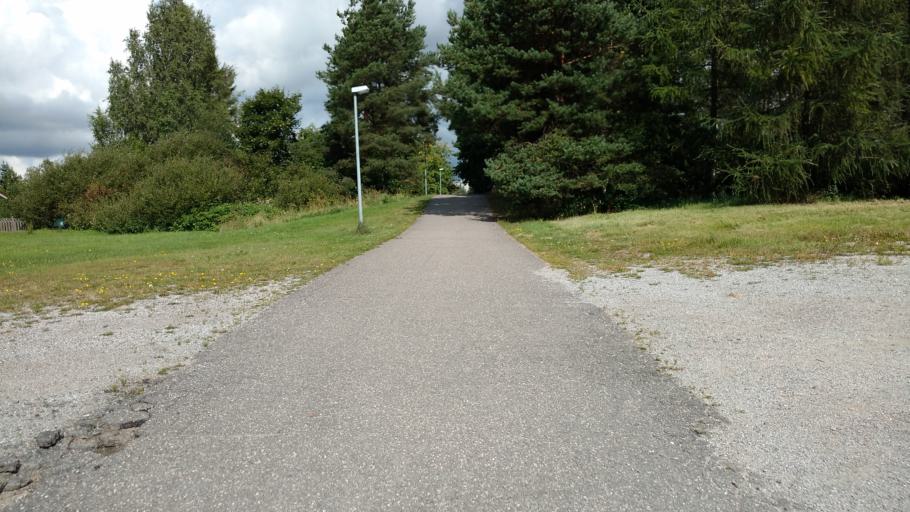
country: FI
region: Varsinais-Suomi
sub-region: Salo
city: Salo
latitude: 60.3681
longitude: 23.1233
